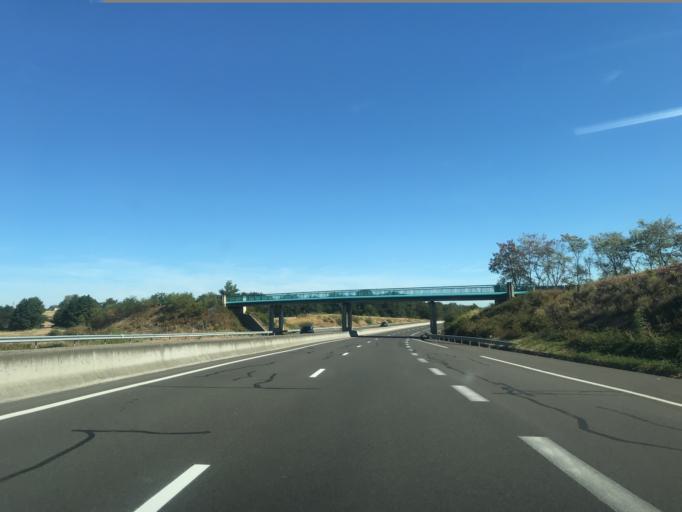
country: FR
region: Auvergne
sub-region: Departement de l'Allier
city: Quinssaines
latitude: 46.3365
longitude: 2.5359
